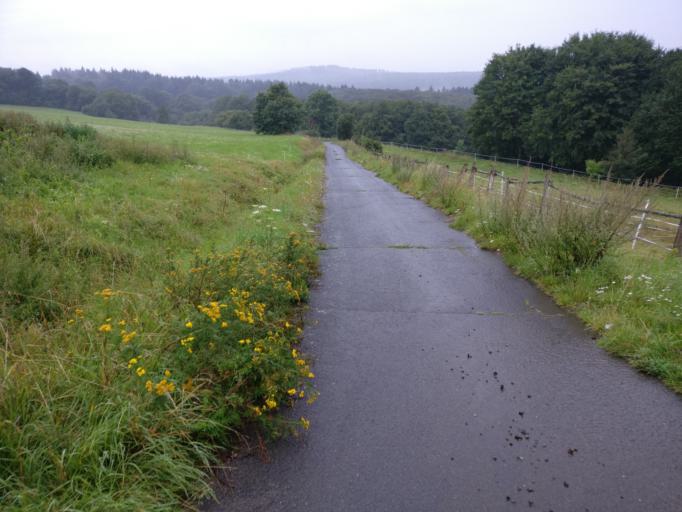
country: DE
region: Hesse
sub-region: Regierungsbezirk Giessen
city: Greifenstein
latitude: 50.6265
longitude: 8.2943
